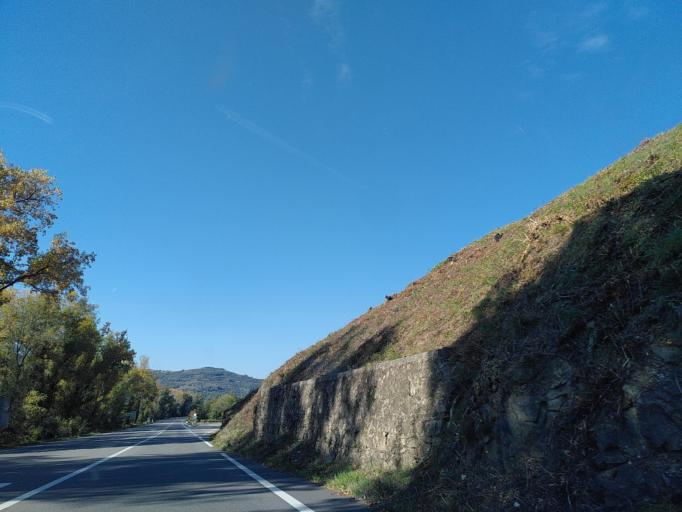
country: FR
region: Rhone-Alpes
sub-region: Departement de la Drome
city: Saint-Vallier
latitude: 45.1639
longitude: 4.8249
